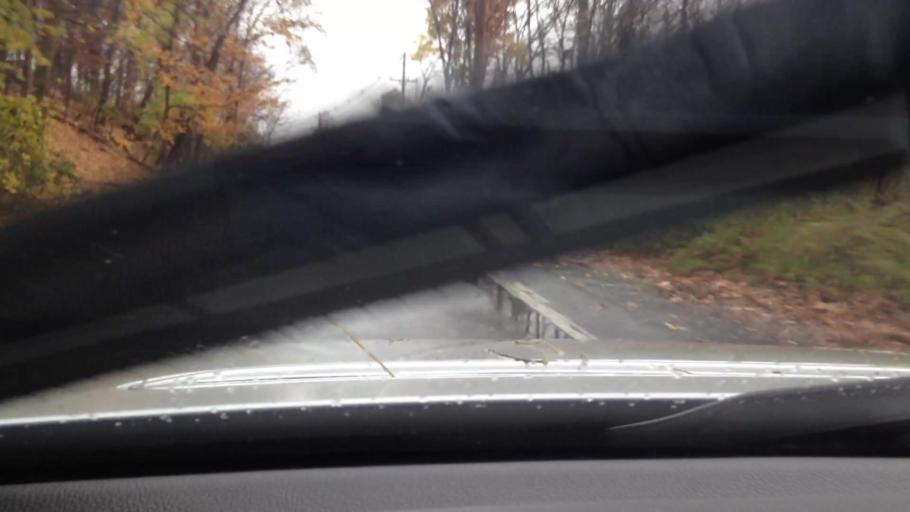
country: US
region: New York
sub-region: Orange County
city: Cornwall-on-Hudson
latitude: 41.4522
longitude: -73.9826
